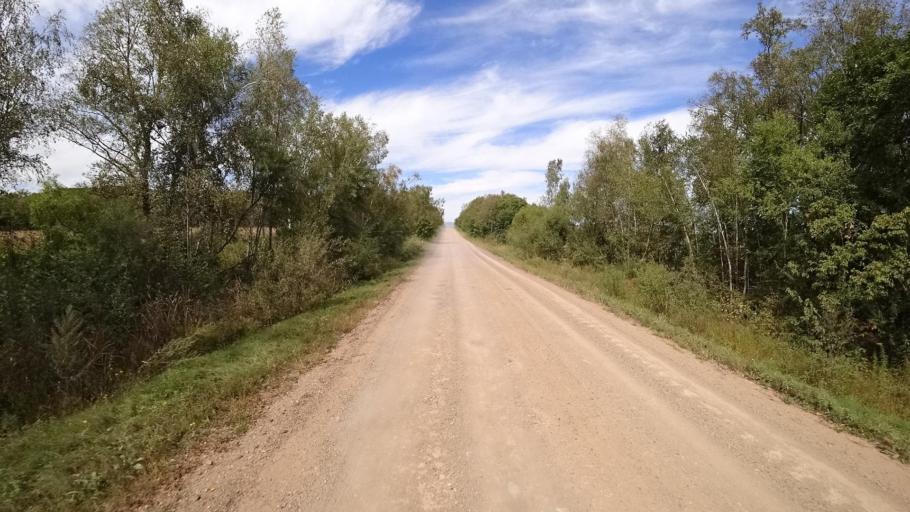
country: RU
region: Primorskiy
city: Yakovlevka
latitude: 44.6016
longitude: 133.6042
